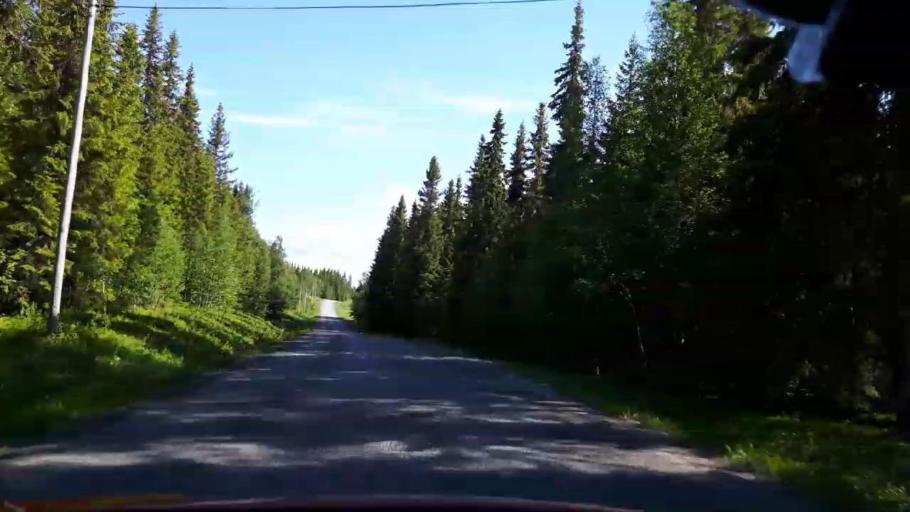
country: SE
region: Jaemtland
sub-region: Krokoms Kommun
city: Valla
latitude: 63.7332
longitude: 14.1176
